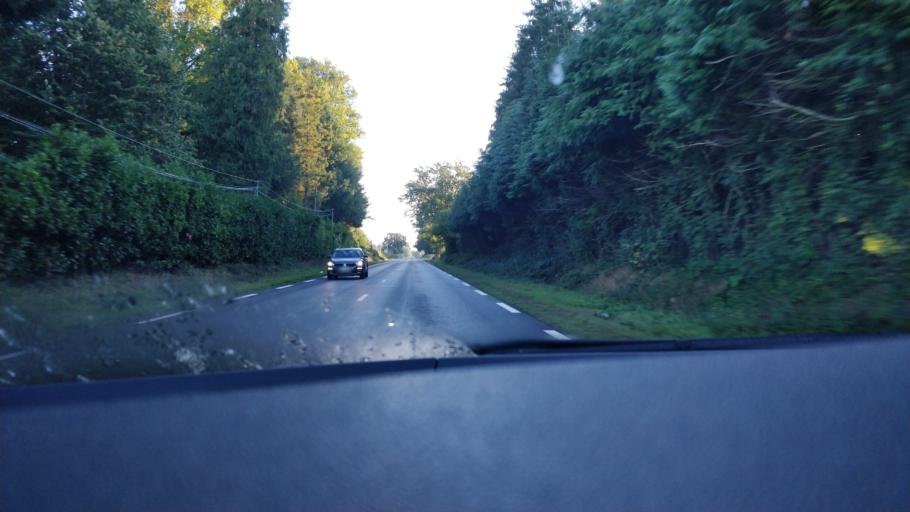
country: FR
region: Limousin
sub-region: Departement de la Haute-Vienne
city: Saint-Leonard-de-Noblat
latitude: 45.8638
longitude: 1.5211
